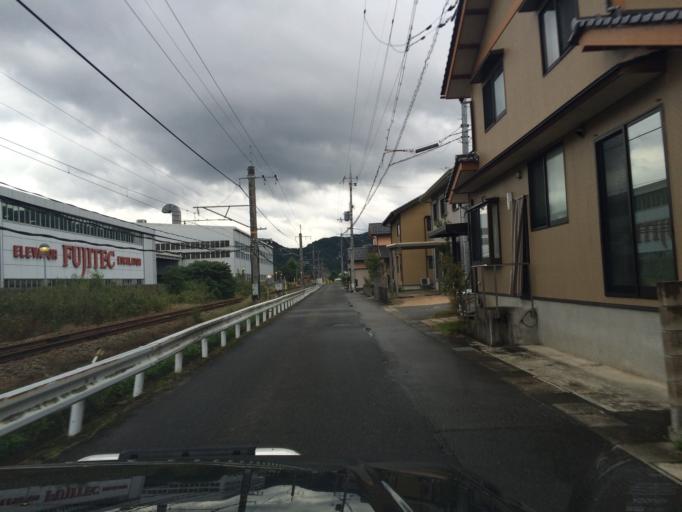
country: JP
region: Hyogo
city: Toyooka
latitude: 35.4655
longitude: 134.7732
